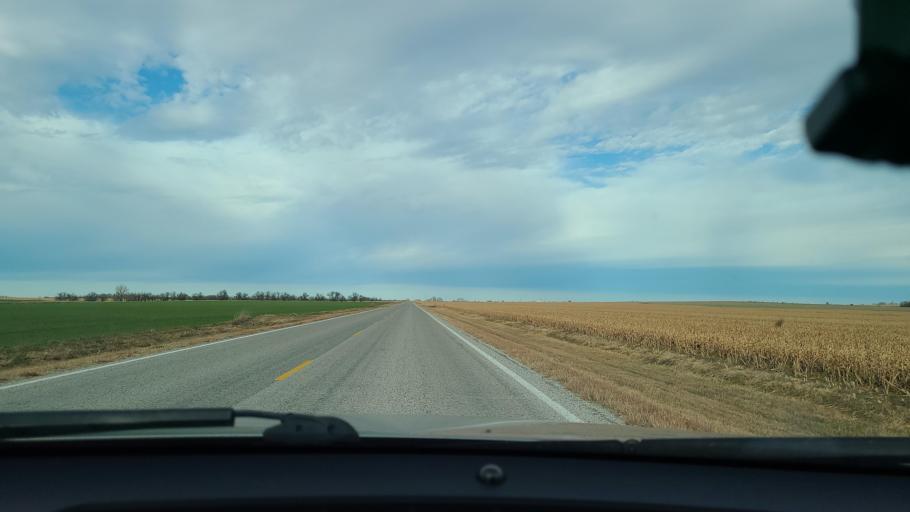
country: US
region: Kansas
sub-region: McPherson County
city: Inman
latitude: 38.3204
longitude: -97.9244
